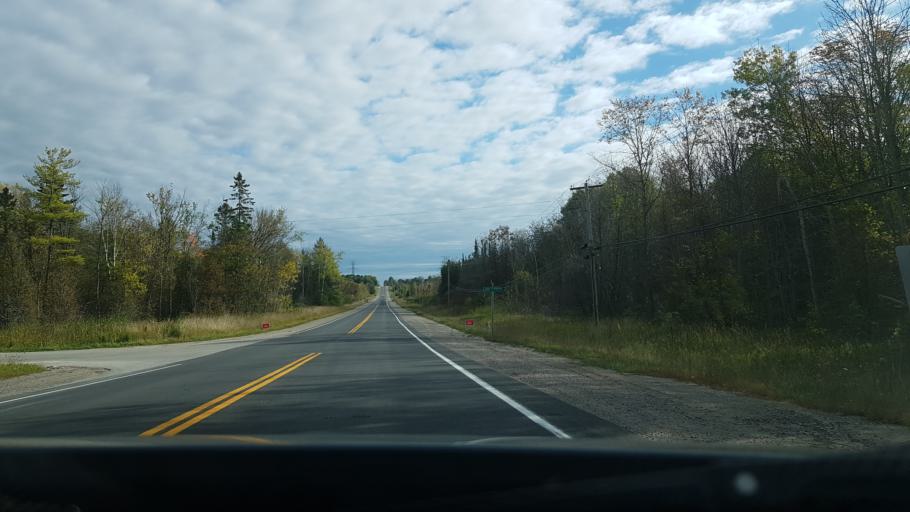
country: CA
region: Ontario
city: Orillia
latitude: 44.6145
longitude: -79.5265
